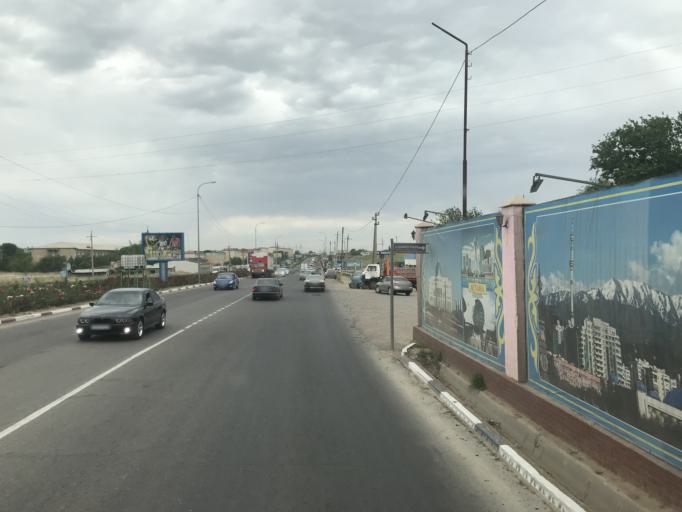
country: KZ
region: Ongtustik Qazaqstan
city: Saryaghash
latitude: 41.4690
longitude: 69.1740
